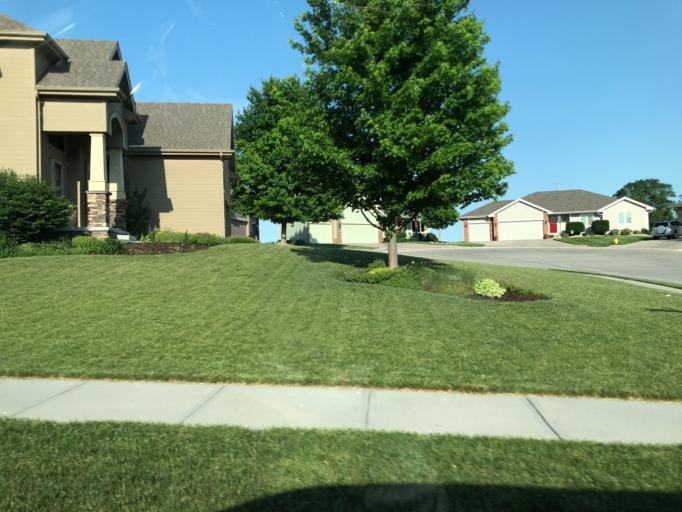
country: US
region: Nebraska
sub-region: Douglas County
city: Elkhorn
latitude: 41.2817
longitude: -96.1883
